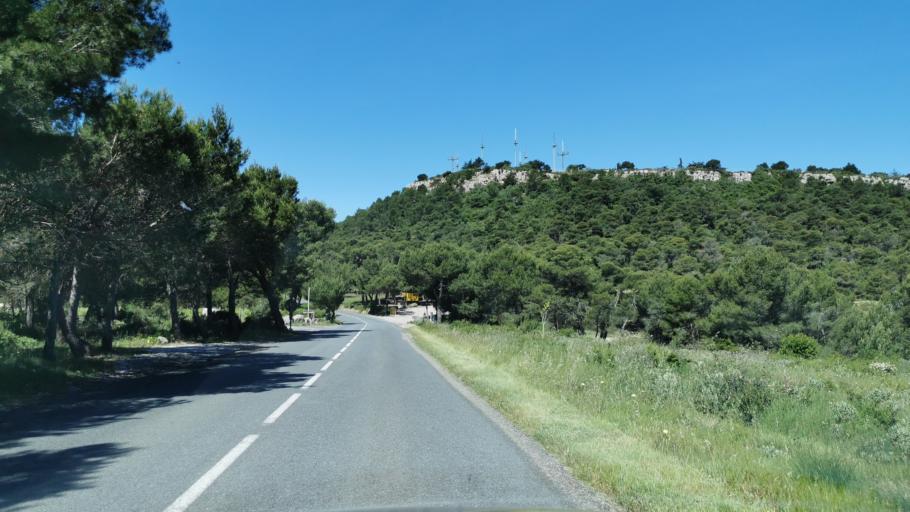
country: FR
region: Languedoc-Roussillon
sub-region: Departement de l'Aude
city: Armissan
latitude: 43.1700
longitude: 3.1234
